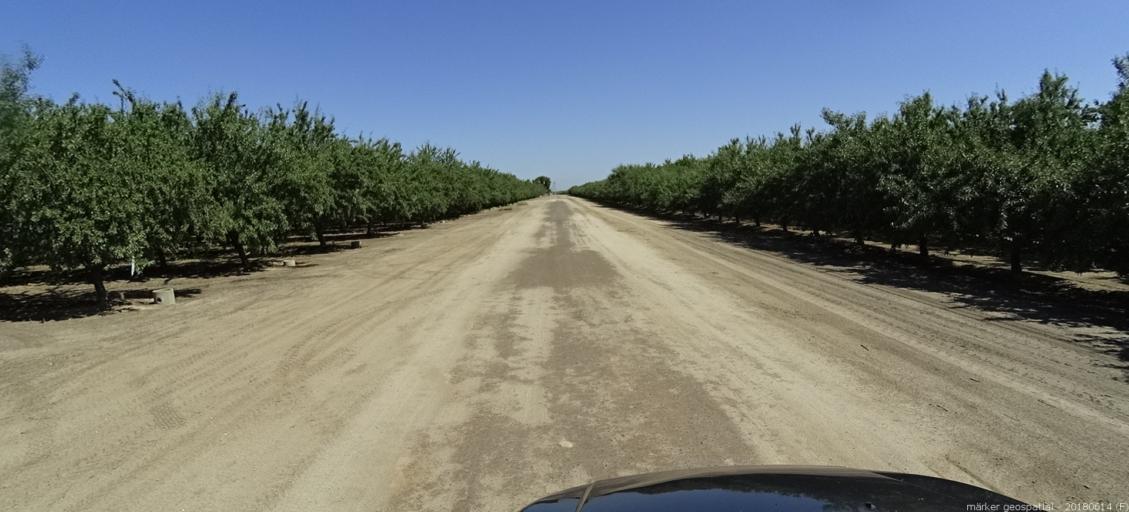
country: US
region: California
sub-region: Madera County
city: Fairmead
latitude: 36.9348
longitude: -120.2242
